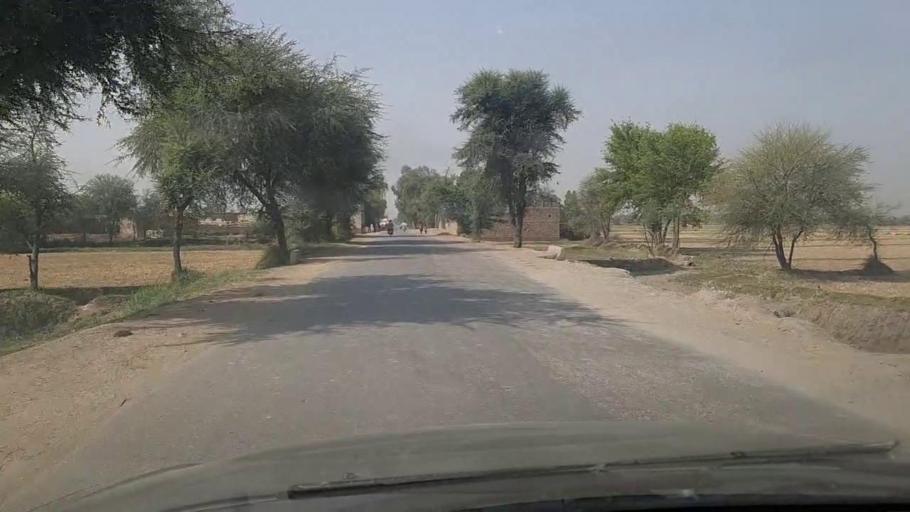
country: PK
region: Sindh
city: Mirpur Mathelo
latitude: 27.9304
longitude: 69.5343
